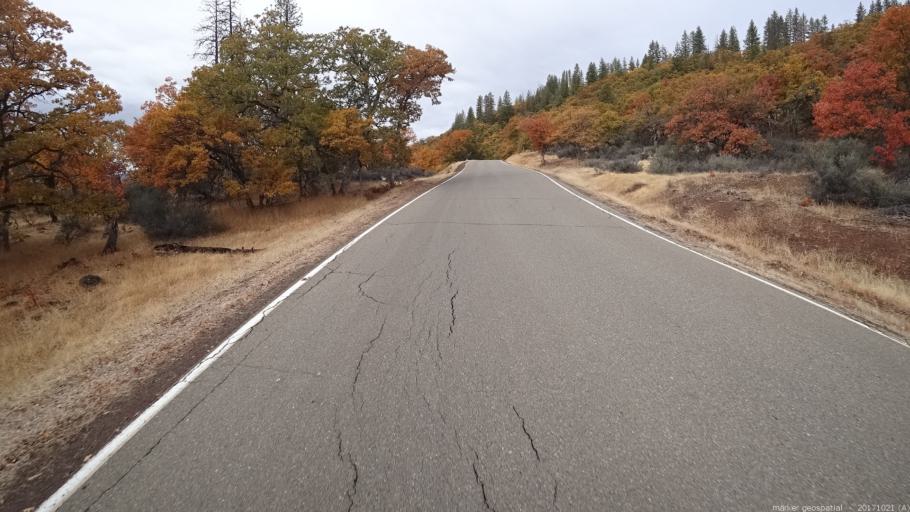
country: US
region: California
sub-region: Shasta County
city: Burney
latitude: 41.0420
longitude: -121.6565
